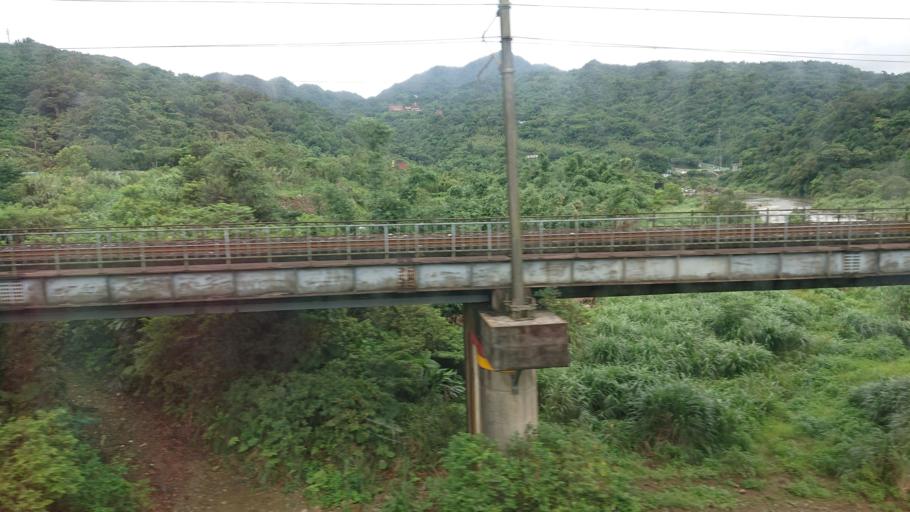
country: TW
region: Taiwan
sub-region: Keelung
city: Keelung
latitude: 25.1059
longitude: 121.8253
